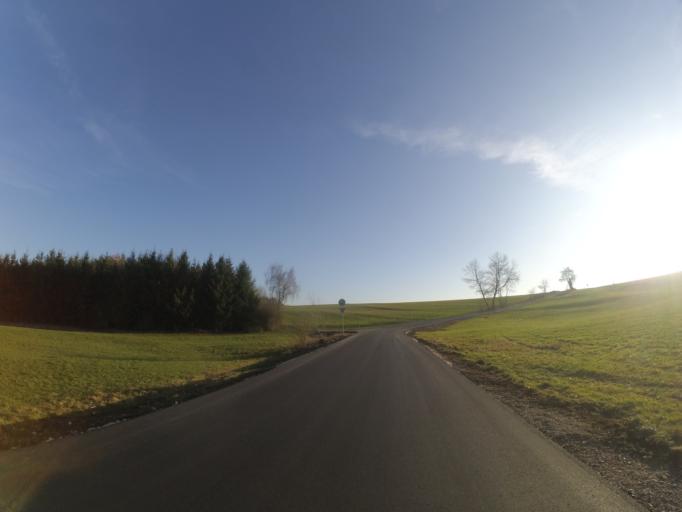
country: DE
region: Baden-Wuerttemberg
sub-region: Tuebingen Region
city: Dornstadt
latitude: 48.4549
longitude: 9.8998
